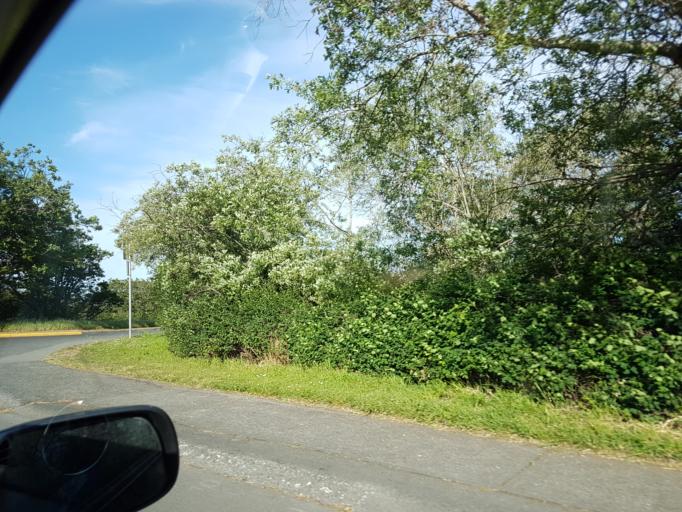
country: CA
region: British Columbia
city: Oak Bay
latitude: 48.4392
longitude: -123.2943
